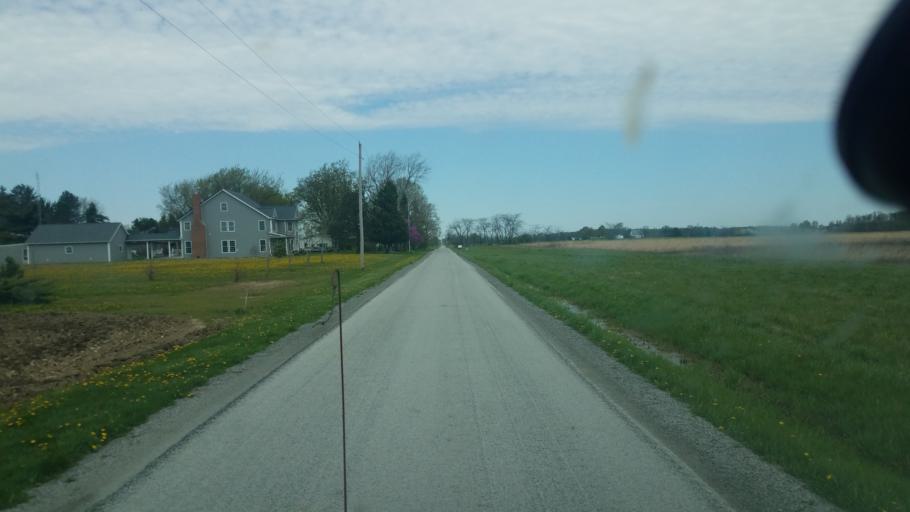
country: US
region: Ohio
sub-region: Hardin County
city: Ada
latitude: 40.7812
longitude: -83.8615
